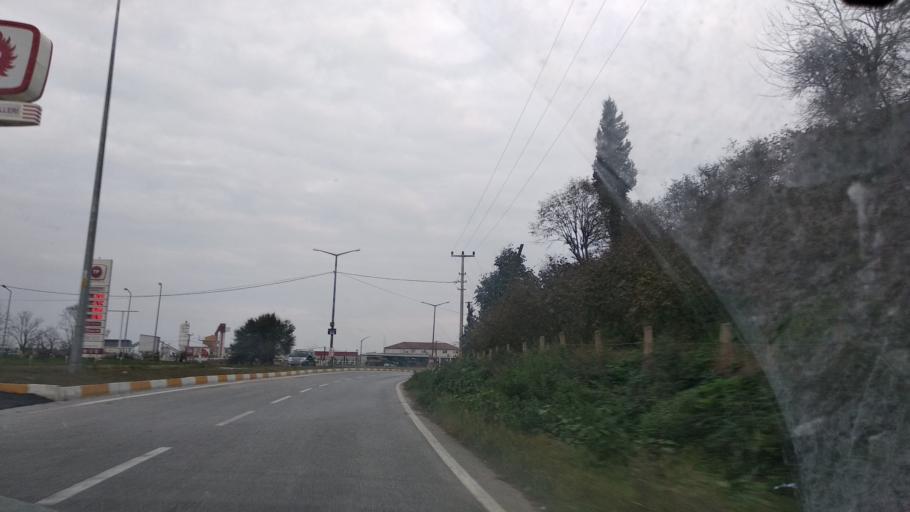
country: TR
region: Sakarya
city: Karasu
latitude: 41.1000
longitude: 30.6684
